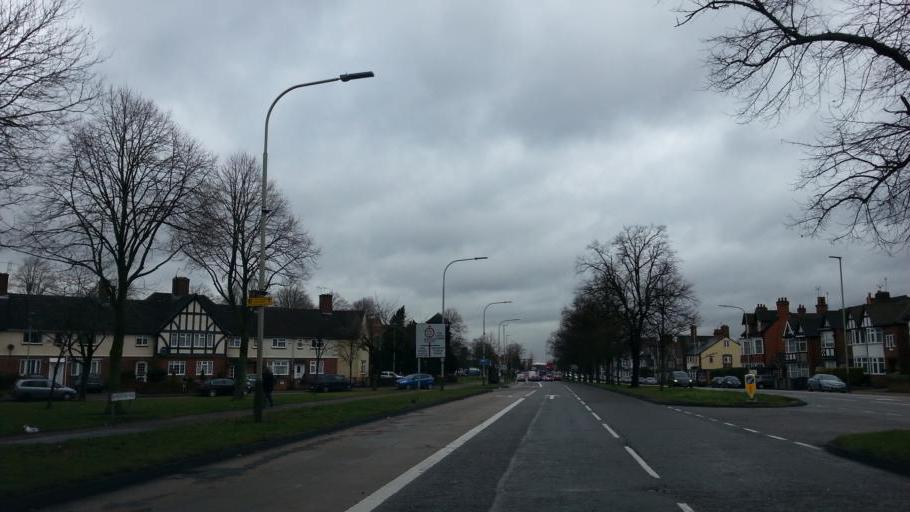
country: GB
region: England
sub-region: City of Leicester
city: Leicester
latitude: 52.6169
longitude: -1.1616
